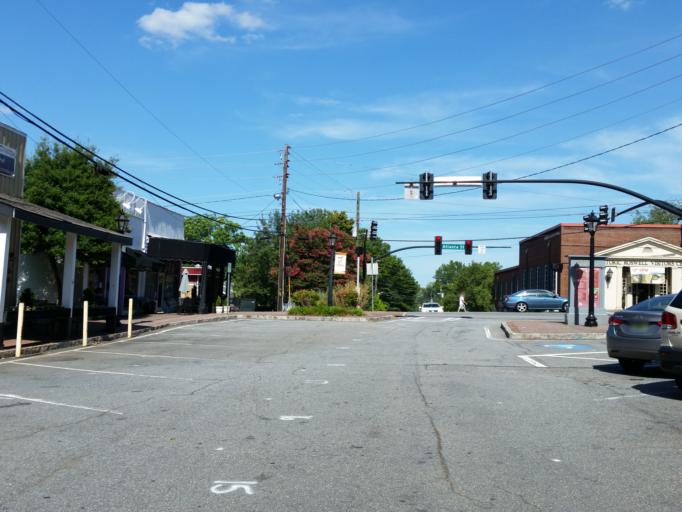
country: US
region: Georgia
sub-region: Fulton County
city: Roswell
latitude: 34.0155
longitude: -84.3634
